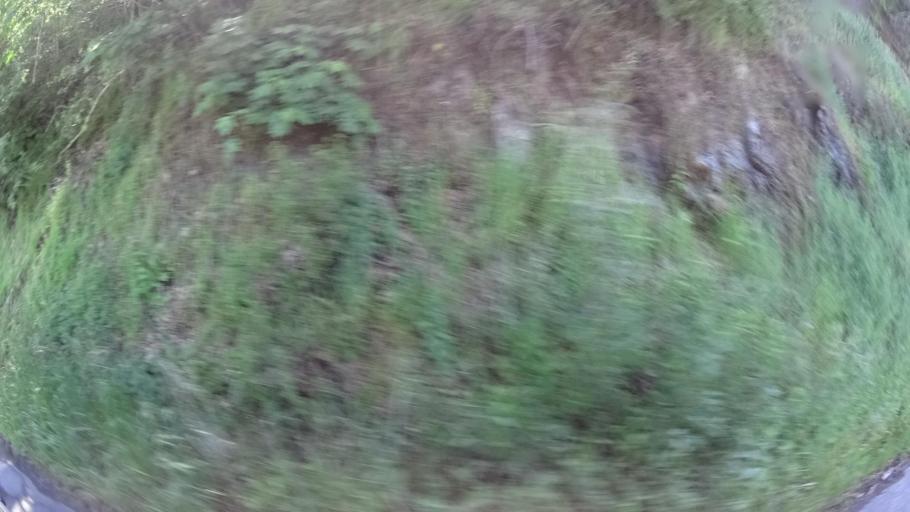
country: US
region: California
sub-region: Humboldt County
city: Rio Dell
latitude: 40.2326
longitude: -124.1380
